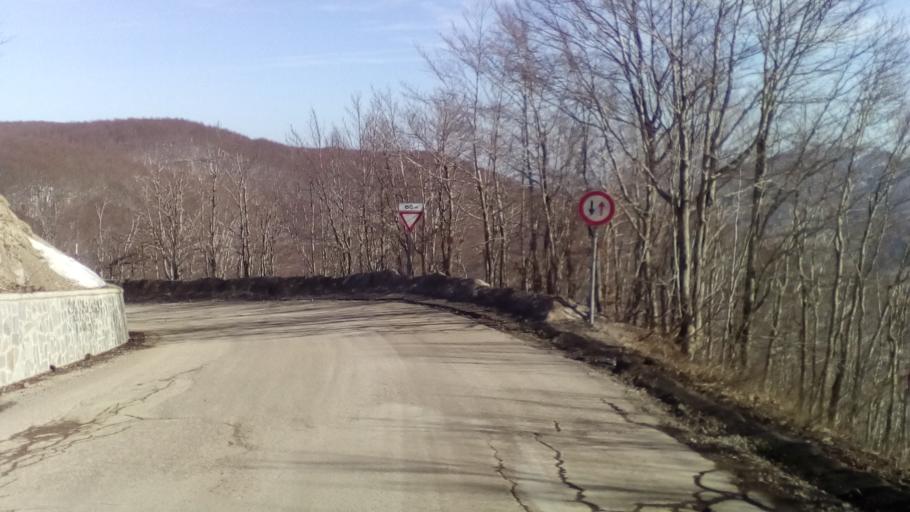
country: IT
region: Tuscany
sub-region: Provincia di Lucca
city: Castiglione di Garfagnana
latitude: 44.2077
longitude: 10.4883
